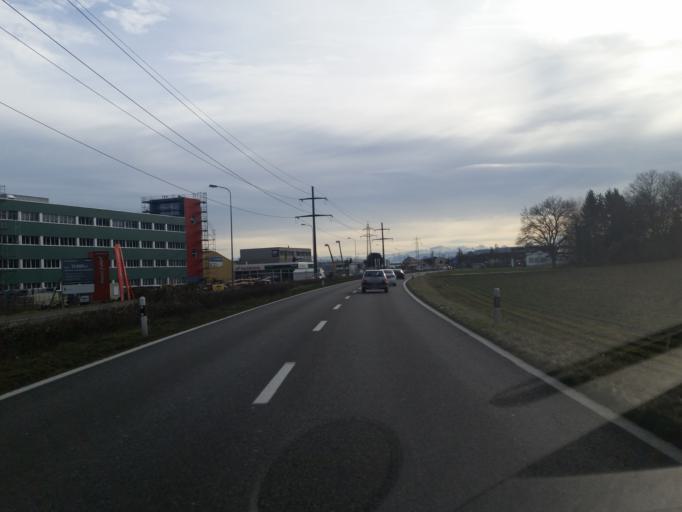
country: CH
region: Aargau
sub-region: Bezirk Bremgarten
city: Dottikon
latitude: 47.3732
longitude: 8.2275
